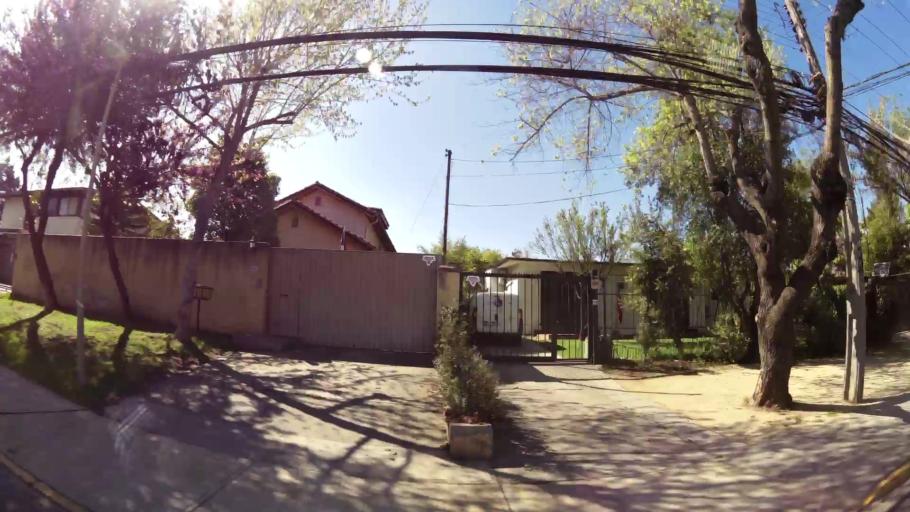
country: CL
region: Santiago Metropolitan
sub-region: Provincia de Santiago
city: Villa Presidente Frei, Nunoa, Santiago, Chile
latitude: -33.3963
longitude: -70.5543
